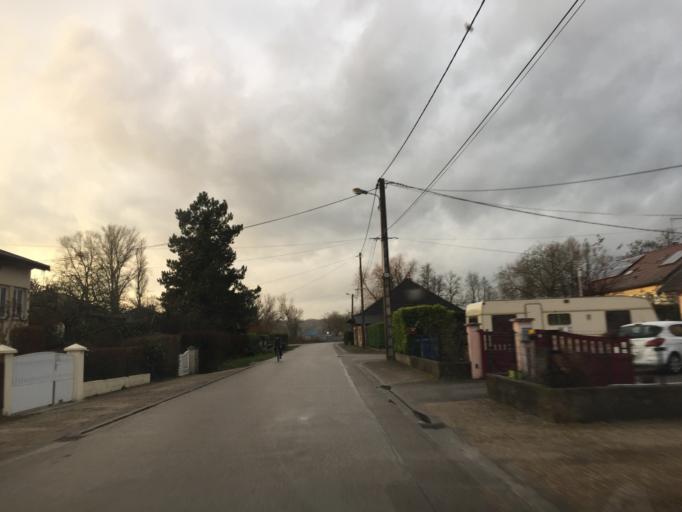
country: FR
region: Franche-Comte
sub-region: Departement du Jura
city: Choisey
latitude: 47.0188
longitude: 5.4832
